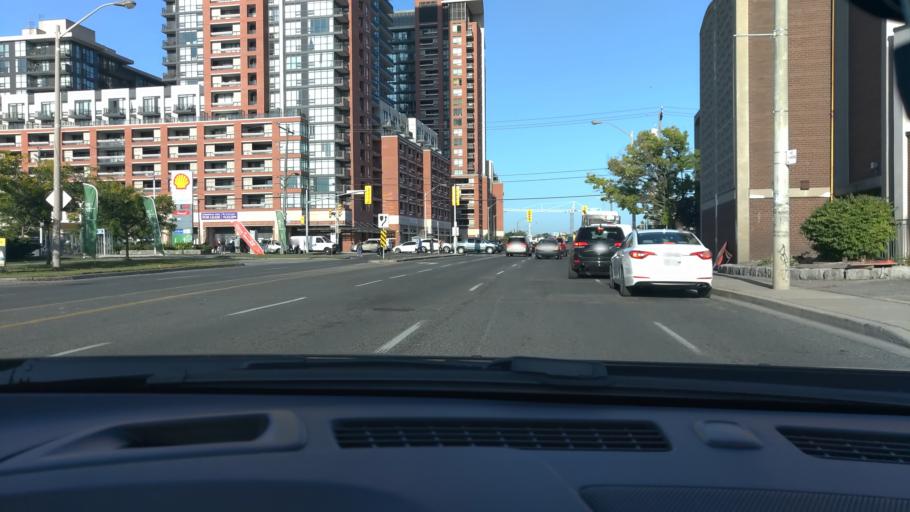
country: CA
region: Ontario
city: Toronto
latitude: 43.7139
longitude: -79.4557
